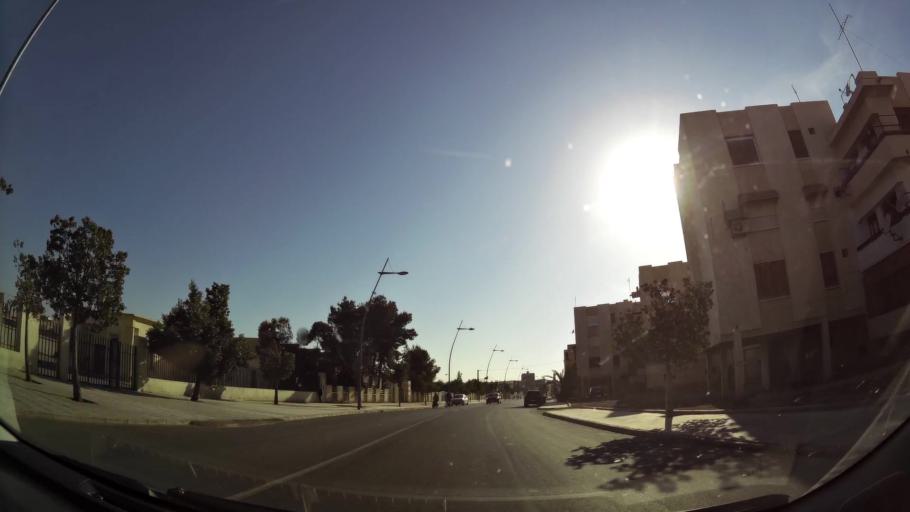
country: MA
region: Oriental
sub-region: Oujda-Angad
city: Oujda
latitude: 34.6977
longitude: -1.9152
